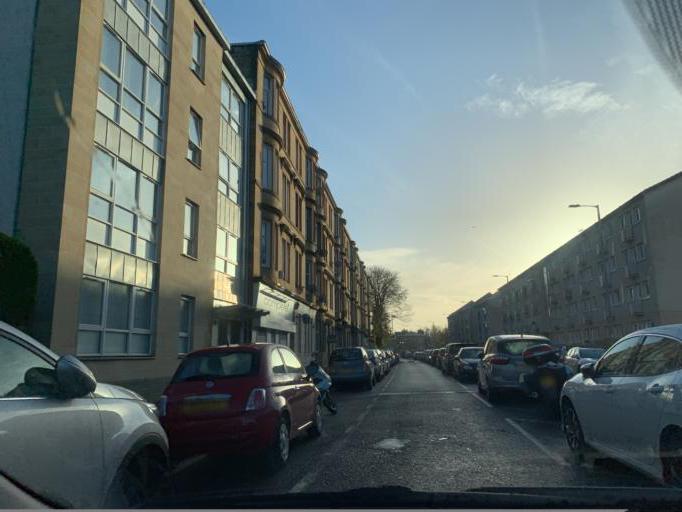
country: GB
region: Scotland
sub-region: East Renfrewshire
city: Giffnock
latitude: 55.8233
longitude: -4.2803
